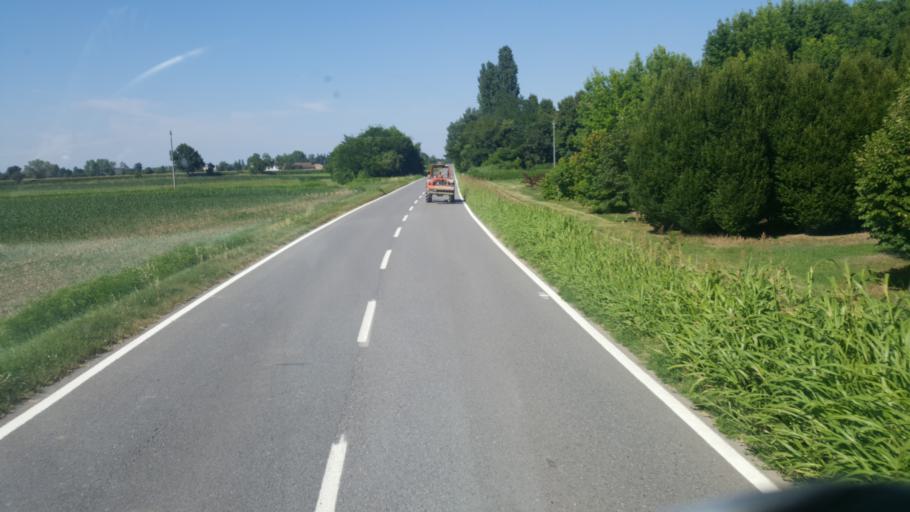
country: IT
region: Lombardy
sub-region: Provincia di Cremona
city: Isola Dovarese
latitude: 45.1816
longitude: 10.3152
